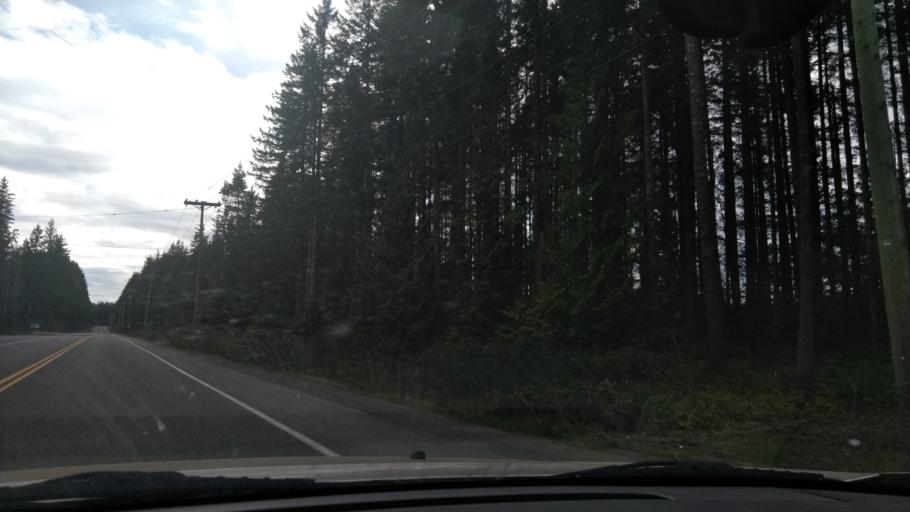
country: CA
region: British Columbia
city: Campbell River
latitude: 50.0176
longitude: -125.3542
